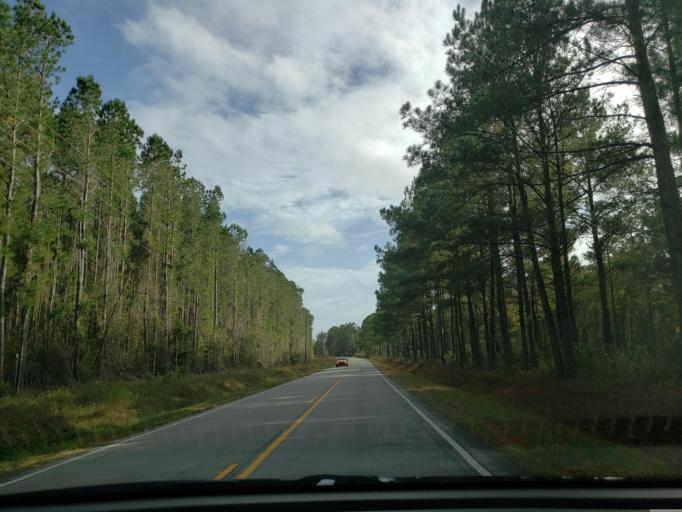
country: US
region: North Carolina
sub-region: Onslow County
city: Jacksonville
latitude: 34.6745
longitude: -77.5007
